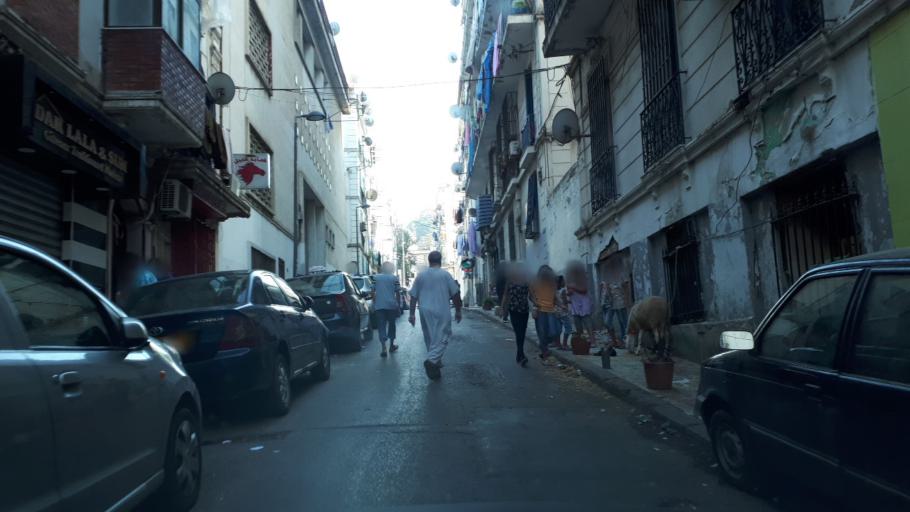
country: DZ
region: Alger
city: Algiers
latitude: 36.7909
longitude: 3.0522
